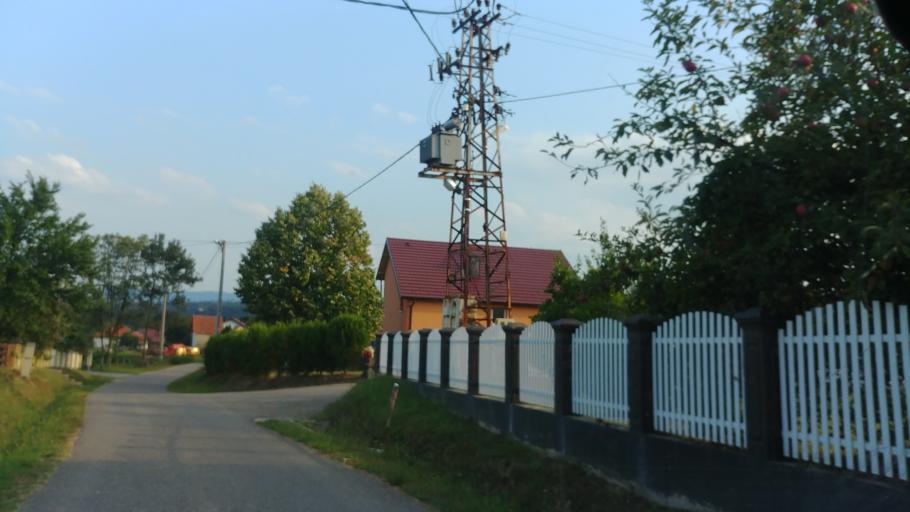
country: BA
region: Republika Srpska
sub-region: Opstina Ugljevik
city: Ugljevik
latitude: 44.7027
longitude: 19.0097
